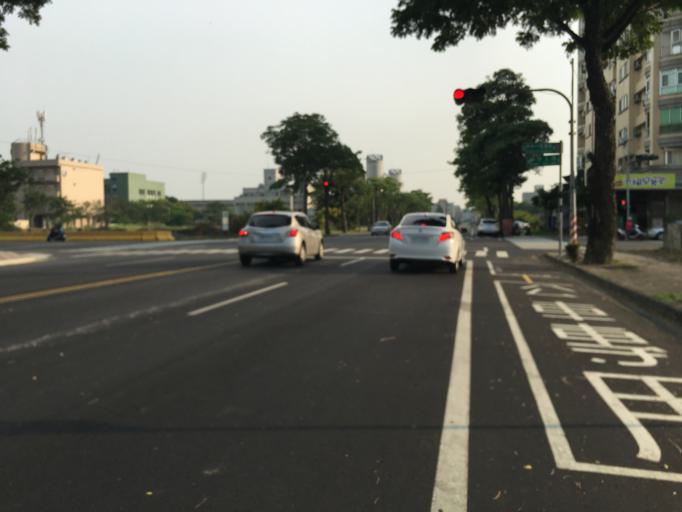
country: TW
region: Taiwan
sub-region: Chiayi
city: Taibao
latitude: 23.4604
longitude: 120.2888
